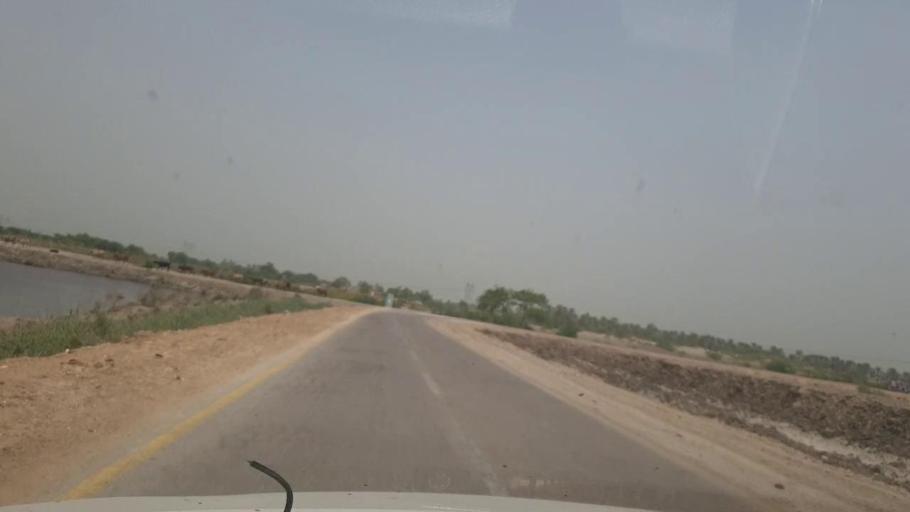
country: PK
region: Sindh
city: Kot Diji
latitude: 27.4031
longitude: 68.6582
